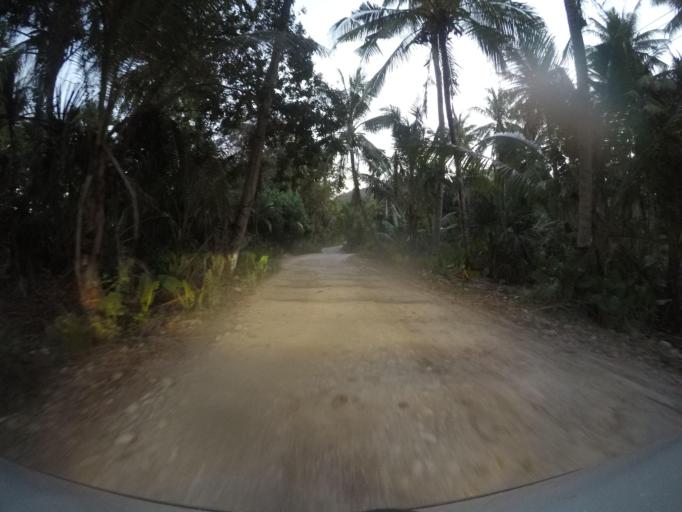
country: TL
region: Viqueque
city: Viqueque
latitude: -8.7900
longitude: 126.6284
